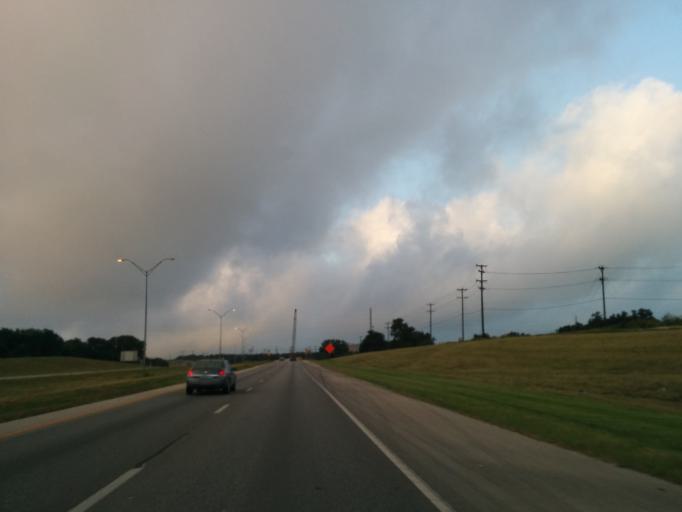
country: US
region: Texas
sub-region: Bexar County
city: Leon Valley
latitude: 29.4872
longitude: -98.7085
